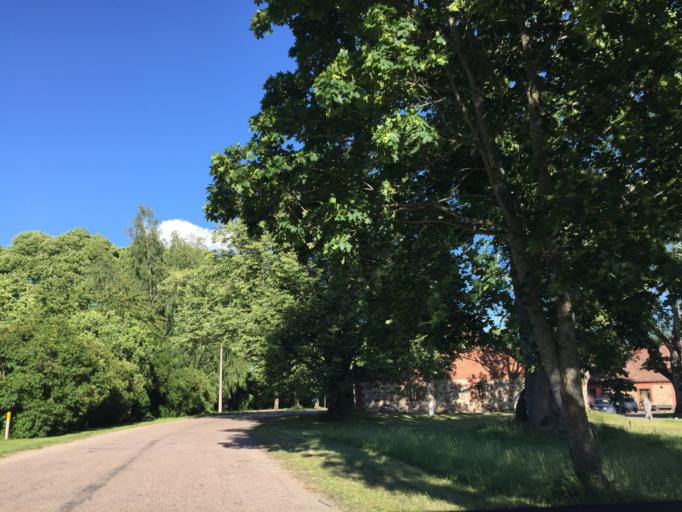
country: LV
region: Ventspils Rajons
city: Piltene
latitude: 57.3975
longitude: 21.8514
